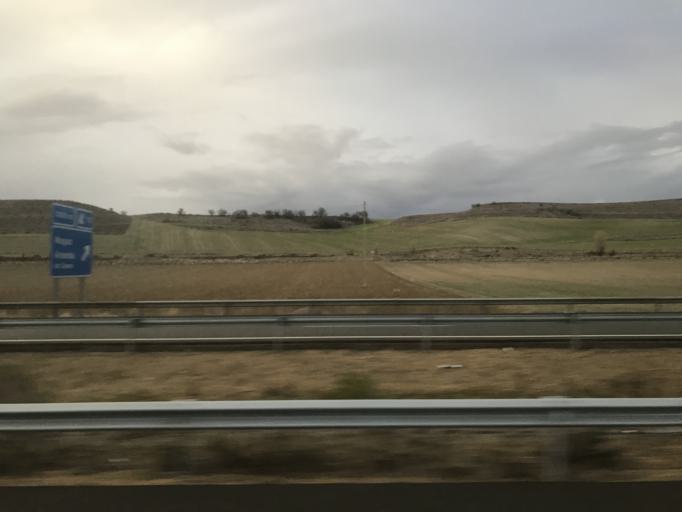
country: ES
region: Castille and Leon
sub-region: Provincia de Palencia
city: Reinoso de Cerrato
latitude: 41.9944
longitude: -4.3946
